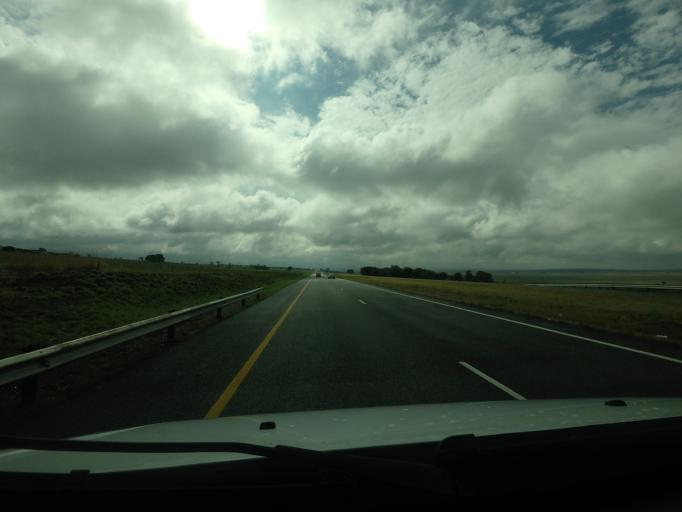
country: ZA
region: Gauteng
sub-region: City of Tshwane Metropolitan Municipality
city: Bronkhorstspruit
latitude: -25.7993
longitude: 28.6339
